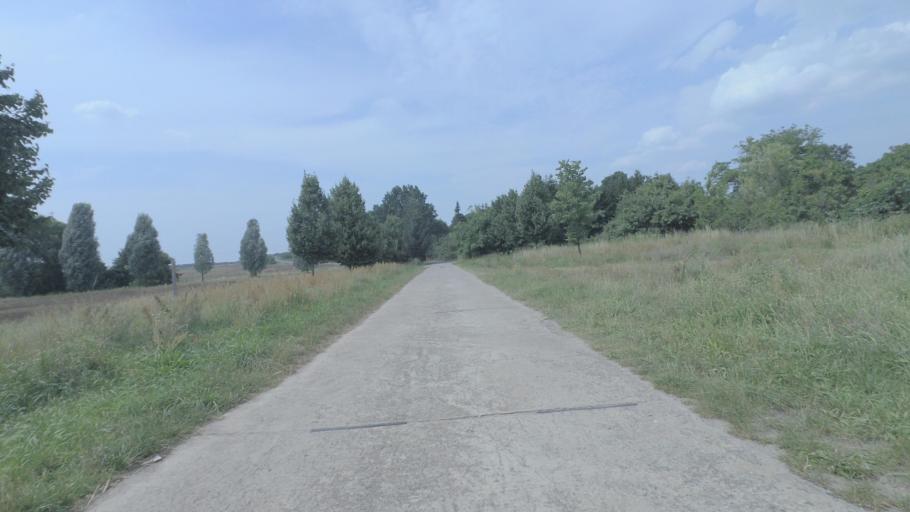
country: DE
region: Brandenburg
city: Rangsdorf
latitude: 52.3400
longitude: 13.4512
